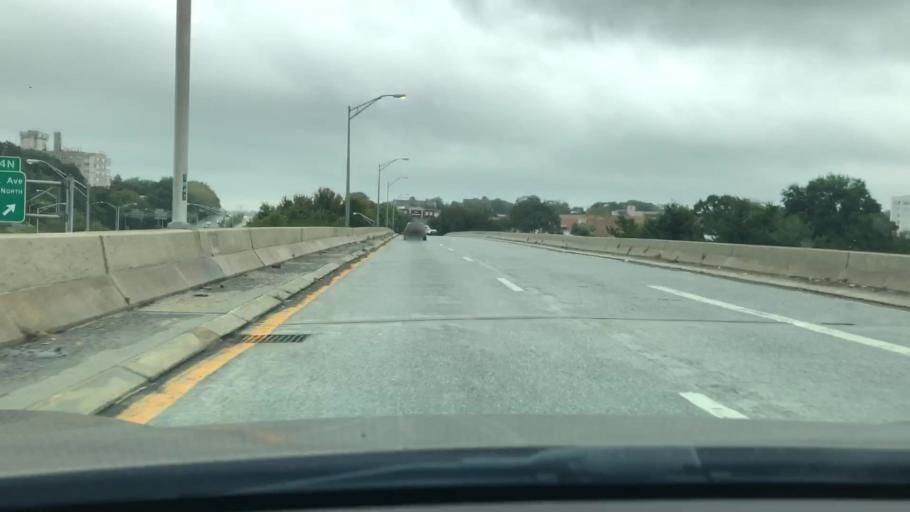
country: US
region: New York
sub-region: Westchester County
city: Bronxville
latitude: 40.9311
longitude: -73.8565
